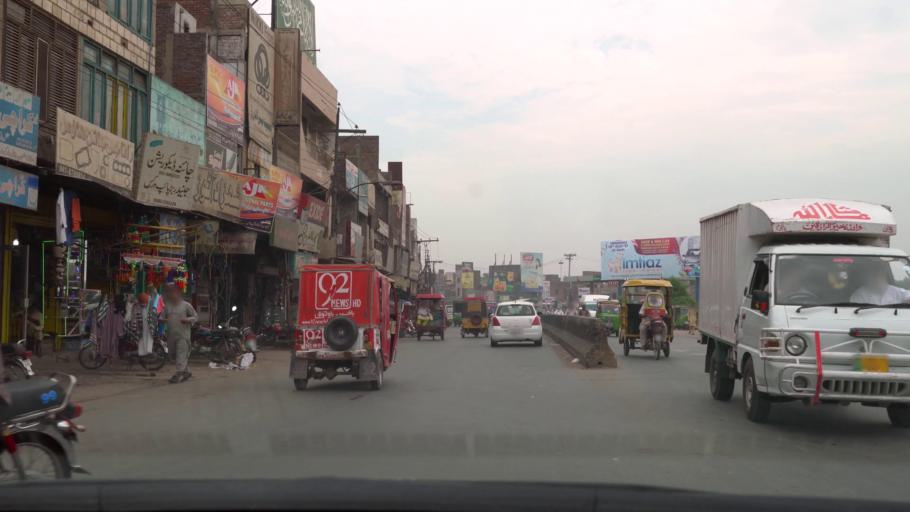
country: PK
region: Punjab
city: Faisalabad
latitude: 31.4284
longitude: 73.0941
